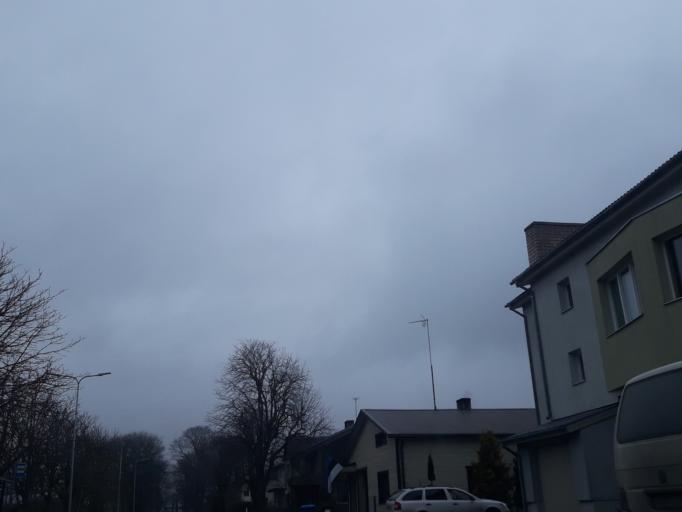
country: EE
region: Saare
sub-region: Kuressaare linn
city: Kuressaare
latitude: 58.2507
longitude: 22.4729
